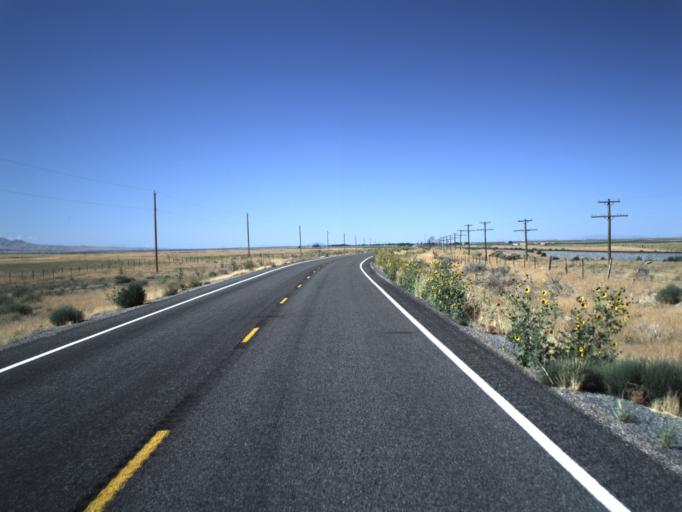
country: US
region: Utah
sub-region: Millard County
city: Delta
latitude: 39.5929
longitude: -112.3290
